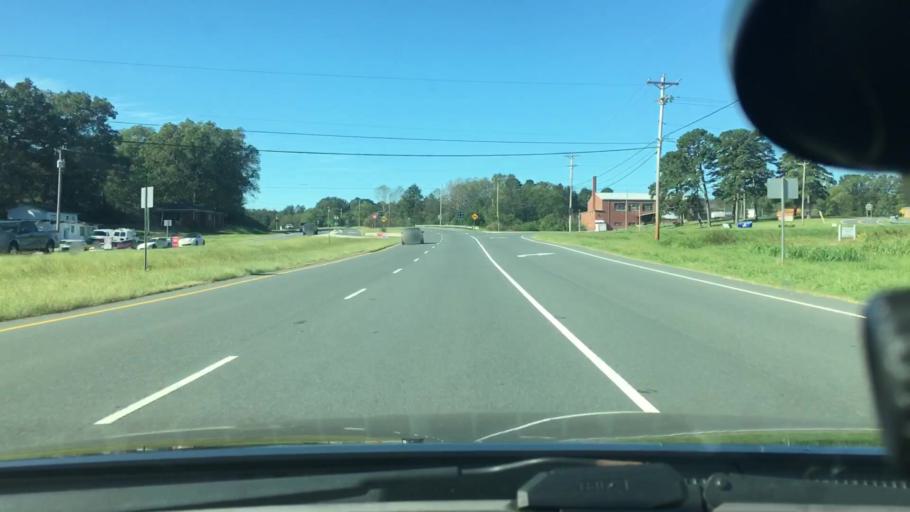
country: US
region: North Carolina
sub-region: Stanly County
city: Albemarle
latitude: 35.3055
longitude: -80.2747
